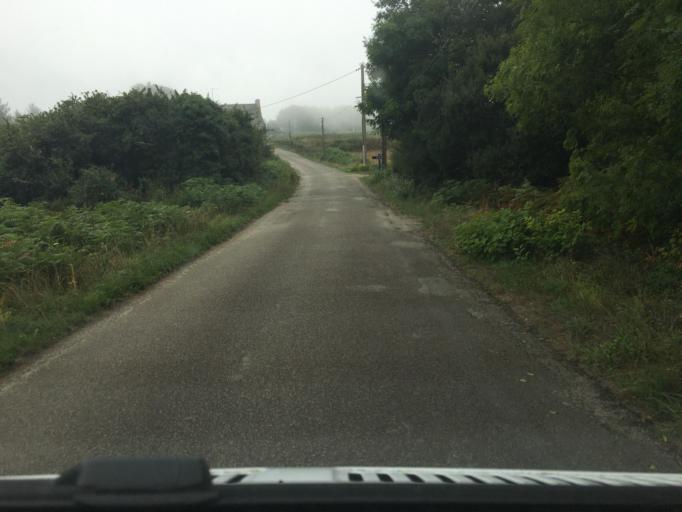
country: FR
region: Brittany
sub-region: Departement du Finistere
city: Plogoff
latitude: 48.0385
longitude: -4.6914
